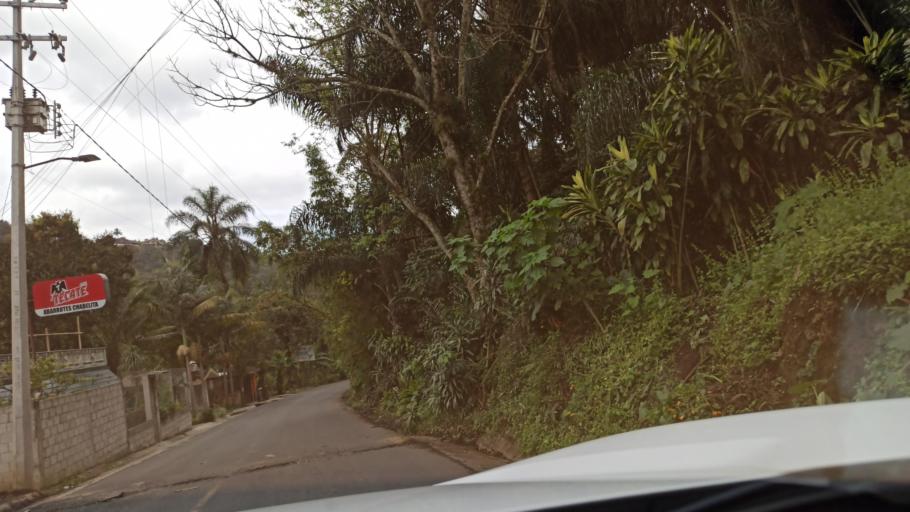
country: MX
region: Veracruz
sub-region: Fortin
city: Fortin de las Flores
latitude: 18.8928
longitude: -97.0077
